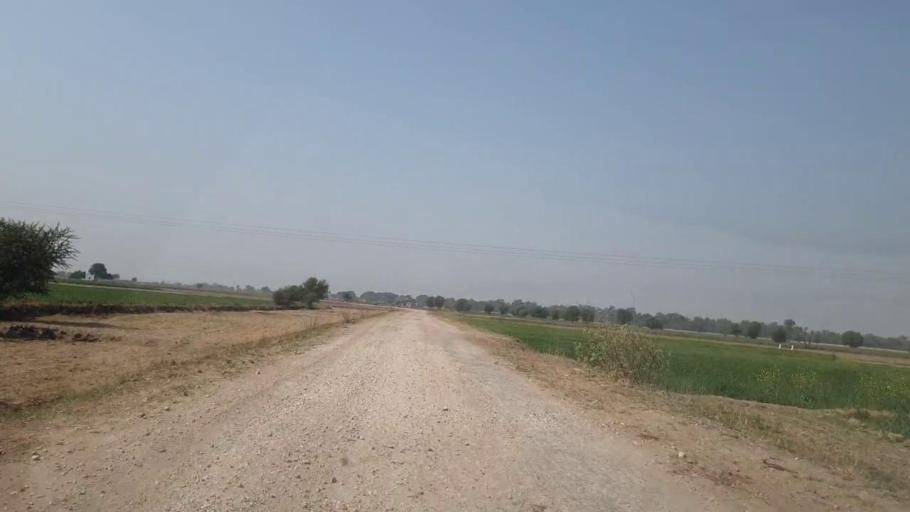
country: PK
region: Sindh
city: Mirpur Khas
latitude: 25.6509
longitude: 69.1080
